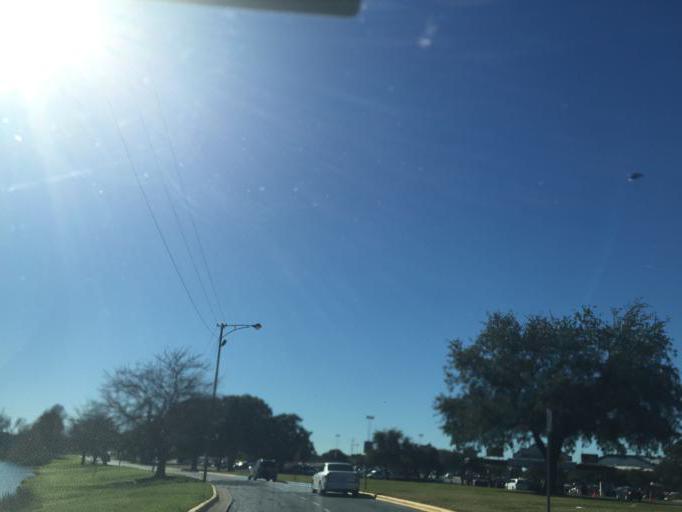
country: US
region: Texas
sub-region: Tarrant County
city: Arlington
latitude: 32.7553
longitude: -97.0692
